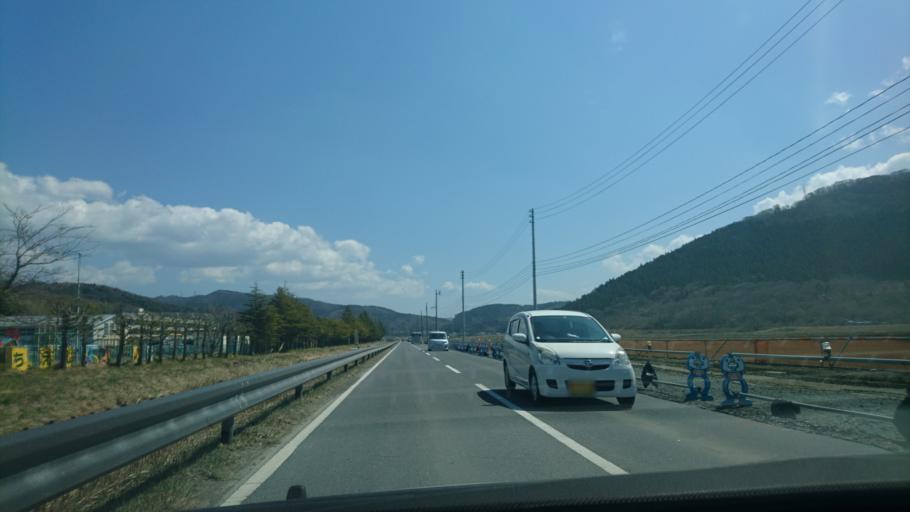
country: JP
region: Miyagi
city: Ishinomaki
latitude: 38.4476
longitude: 141.3541
